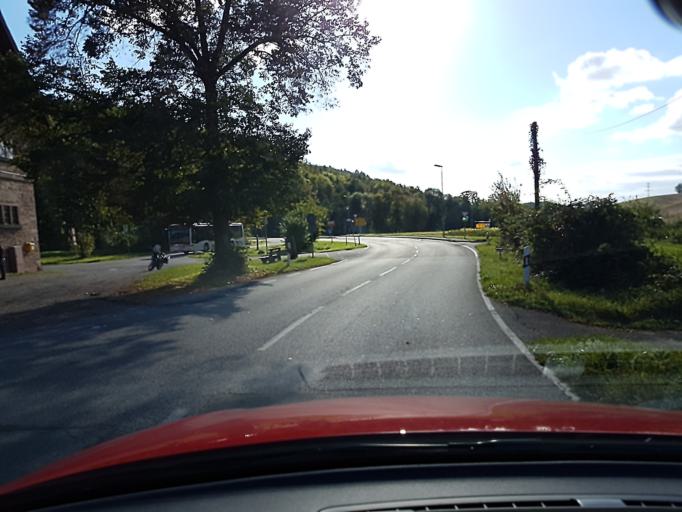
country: DE
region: Baden-Wuerttemberg
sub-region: Karlsruhe Region
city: Wiesenbach
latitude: 49.3641
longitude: 8.8380
